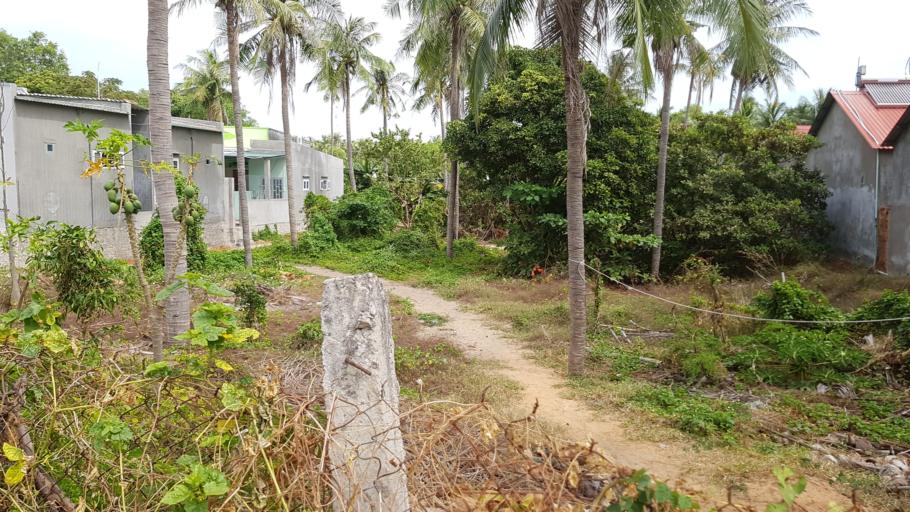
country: VN
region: Binh Thuan
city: Phan Thiet
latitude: 10.9484
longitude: 108.2002
